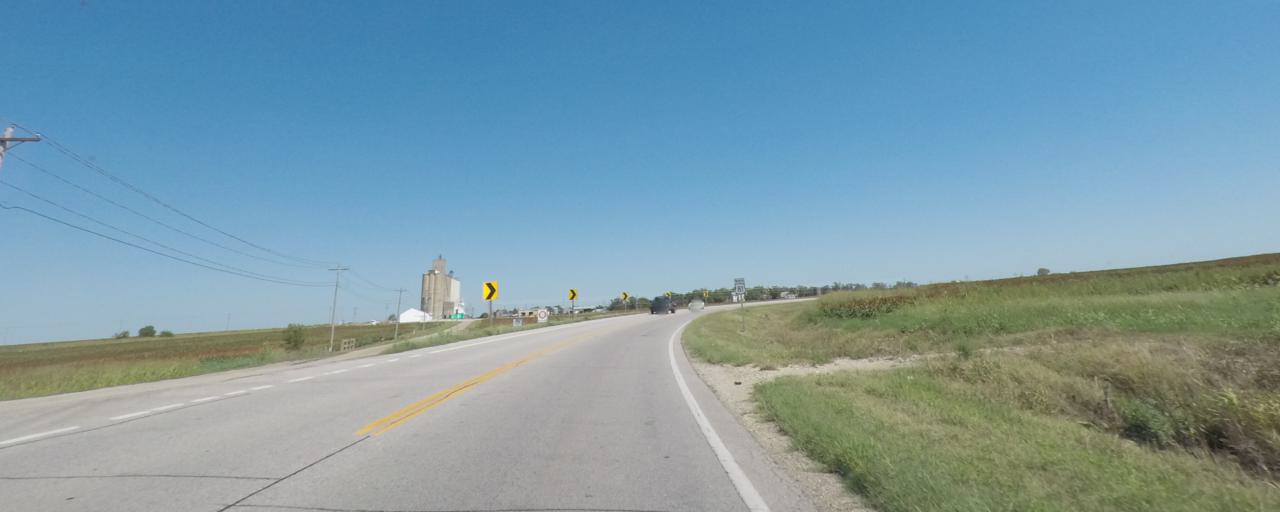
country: US
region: Kansas
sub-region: Sumner County
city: Wellington
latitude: 37.2994
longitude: -97.3944
